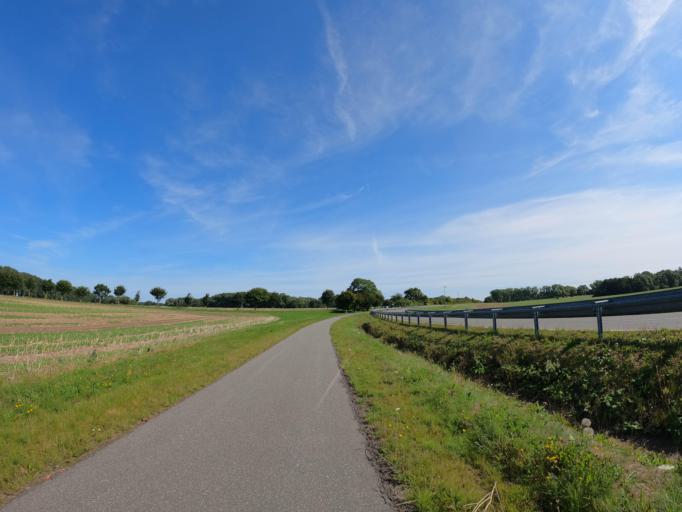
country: DE
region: Mecklenburg-Vorpommern
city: Kramerhof
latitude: 54.3600
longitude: 13.0614
